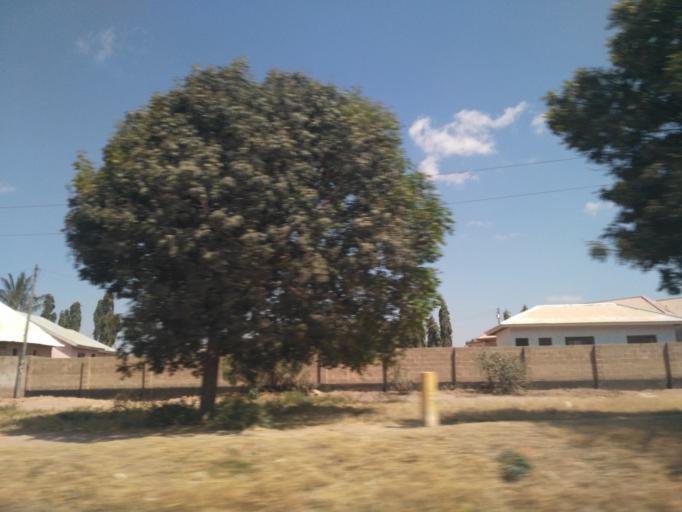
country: TZ
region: Dodoma
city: Dodoma
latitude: -6.1549
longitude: 35.7235
